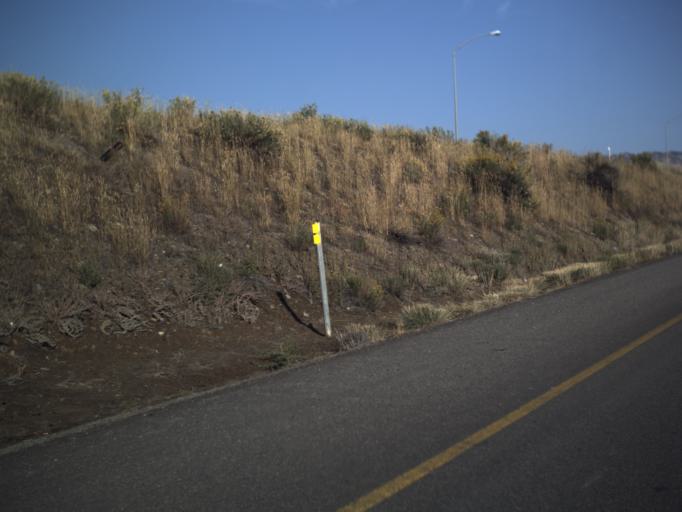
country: US
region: Utah
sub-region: Carbon County
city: Price
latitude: 39.6020
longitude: -110.8277
